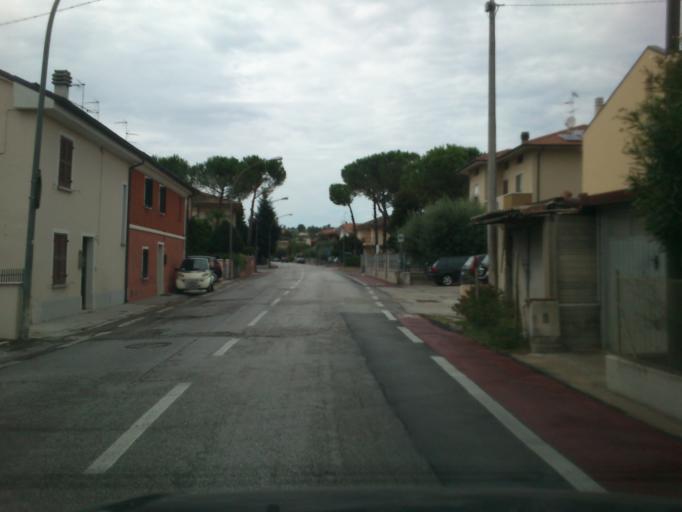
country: IT
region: The Marches
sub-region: Provincia di Pesaro e Urbino
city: Lucrezia
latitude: 43.7766
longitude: 12.9433
